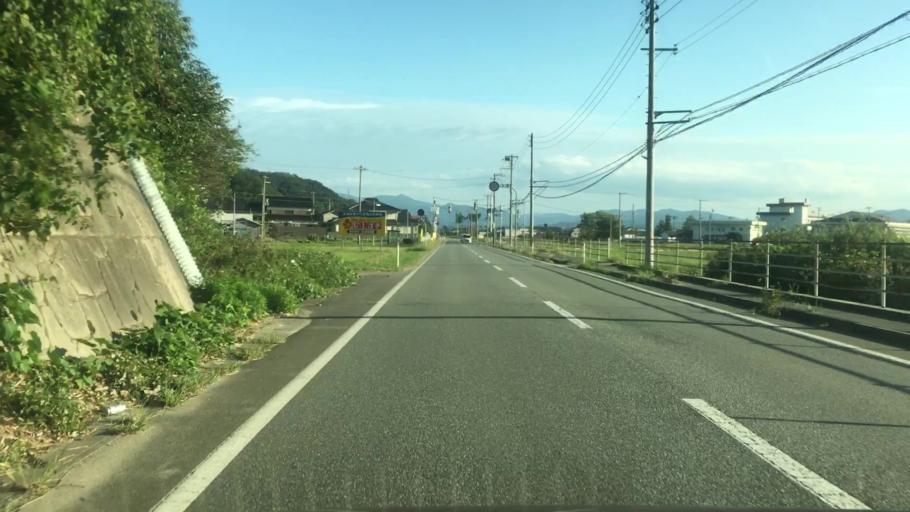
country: JP
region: Hyogo
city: Toyooka
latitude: 35.5663
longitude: 134.8195
